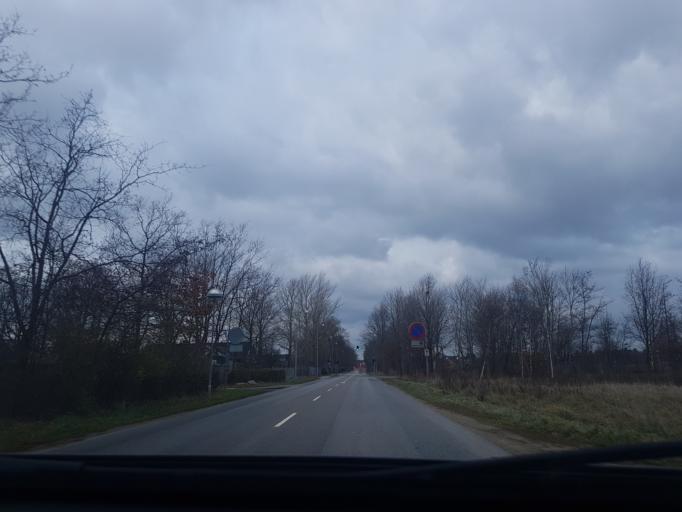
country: DK
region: Capital Region
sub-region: Ishoj Kommune
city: Ishoj
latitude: 55.6093
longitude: 12.3733
